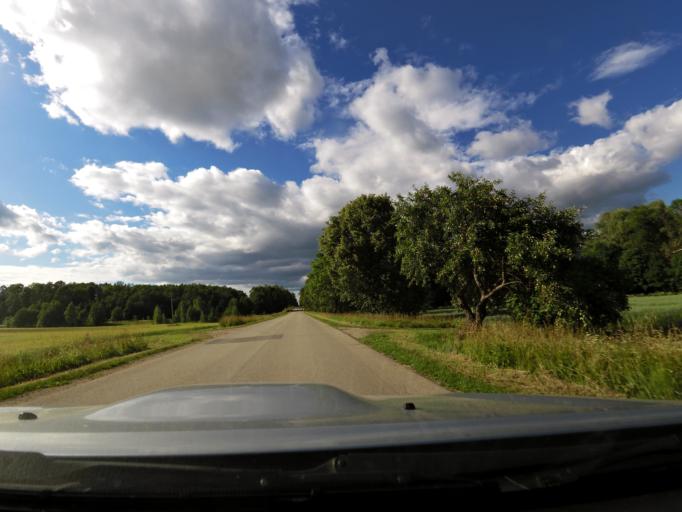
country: LT
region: Panevezys
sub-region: Birzai
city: Birzai
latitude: 56.3508
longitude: 24.7931
